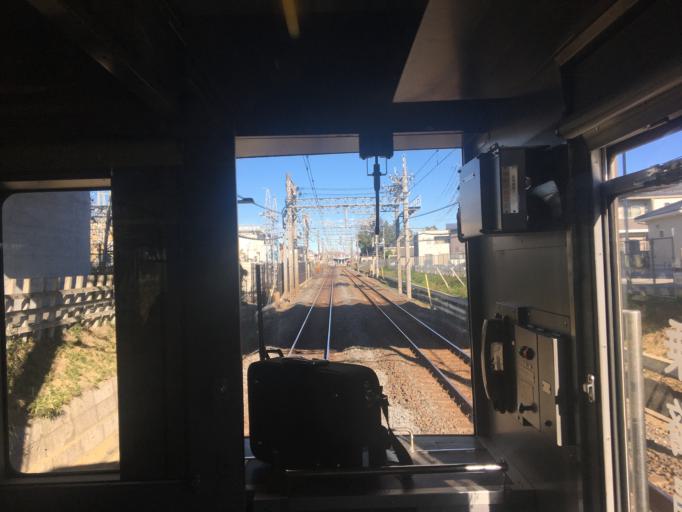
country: JP
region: Saitama
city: Sakado
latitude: 35.9981
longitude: 139.3991
